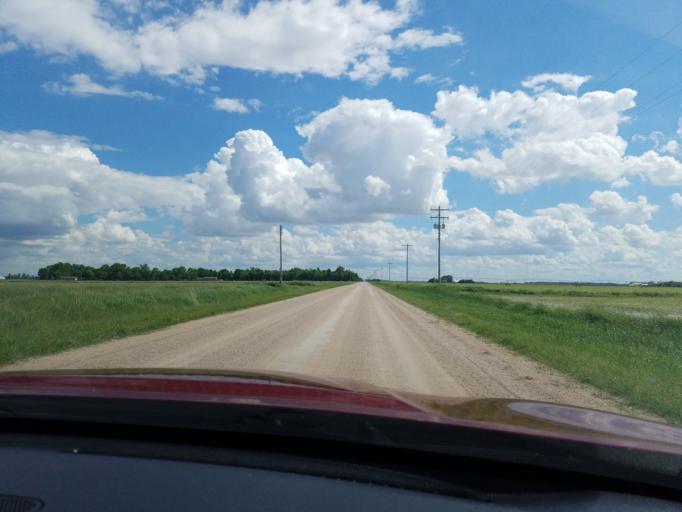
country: US
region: Nebraska
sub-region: Buffalo County
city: Kearney
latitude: 40.6508
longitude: -99.0085
